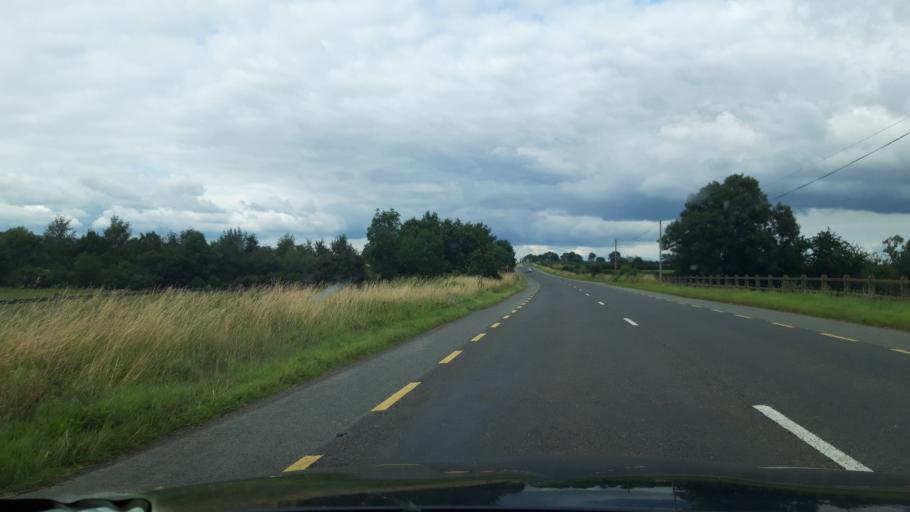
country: IE
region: Leinster
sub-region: County Carlow
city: Bagenalstown
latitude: 52.6691
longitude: -7.0280
